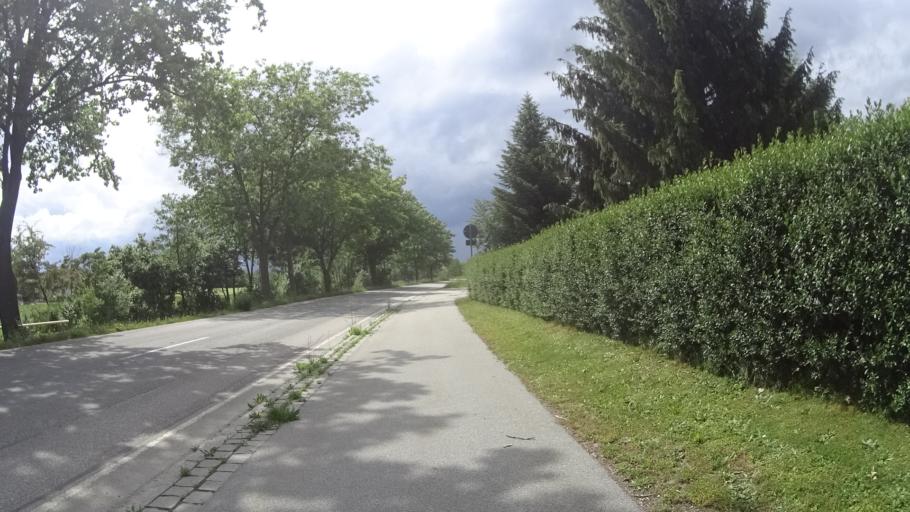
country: DE
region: Bavaria
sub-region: Upper Bavaria
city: Egglkofen
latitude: 48.4475
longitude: 12.4962
